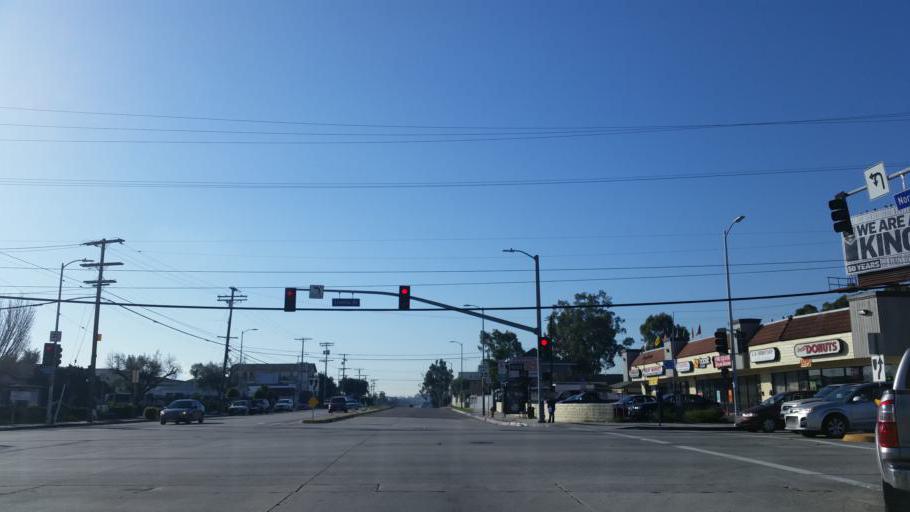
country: US
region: California
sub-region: Los Angeles County
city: Lomita
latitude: 33.7980
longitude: -118.2976
